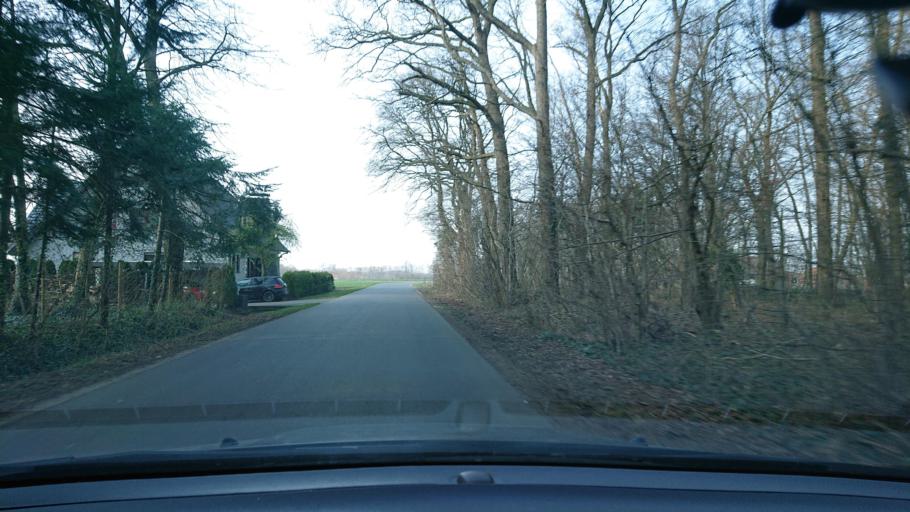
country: DE
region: North Rhine-Westphalia
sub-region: Regierungsbezirk Detmold
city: Langenberg
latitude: 51.7630
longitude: 8.3720
